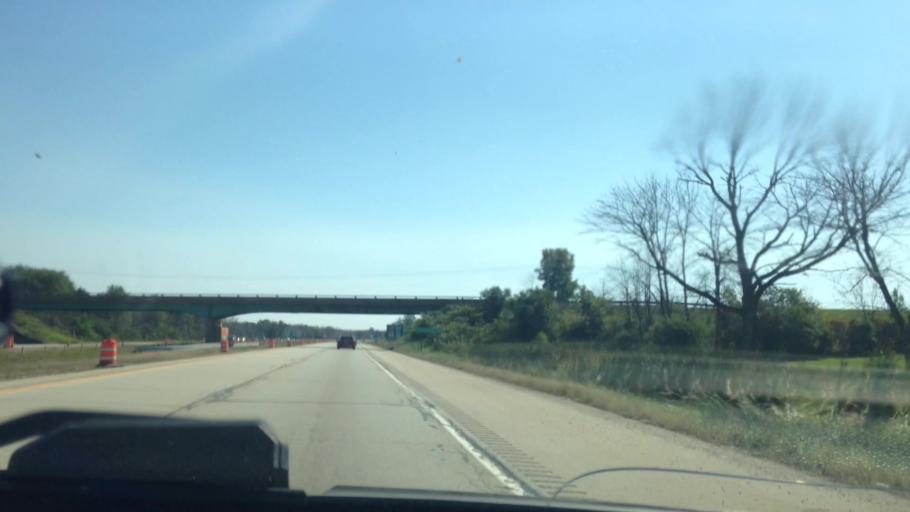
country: US
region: Wisconsin
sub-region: Ozaukee County
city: Grafton
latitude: 43.3323
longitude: -87.9229
